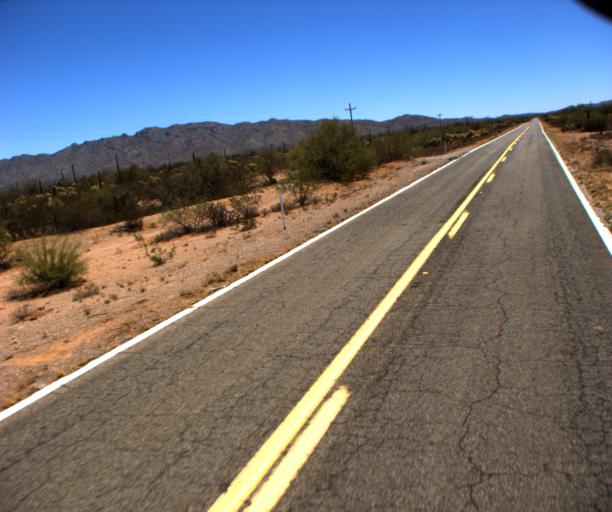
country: US
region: Arizona
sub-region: Pima County
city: Sells
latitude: 32.1831
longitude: -112.3023
